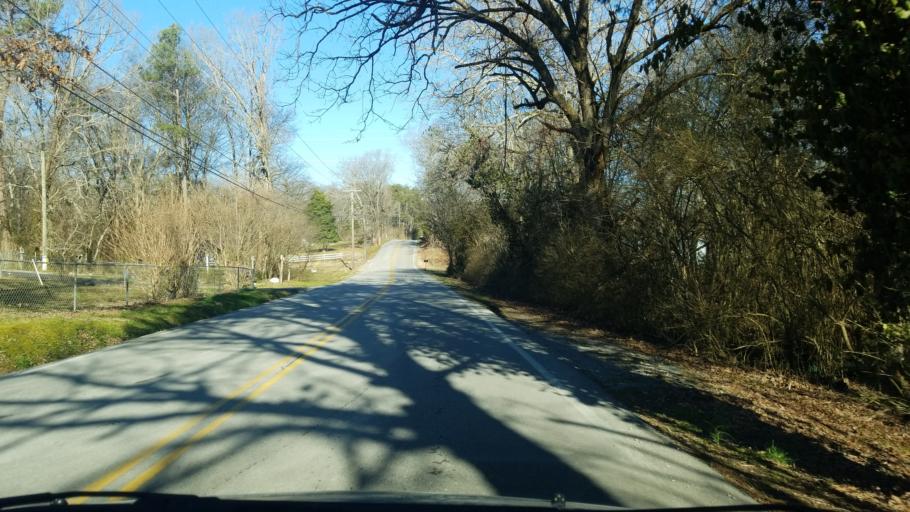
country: US
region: Tennessee
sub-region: Hamilton County
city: Collegedale
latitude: 35.0593
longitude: -85.0943
